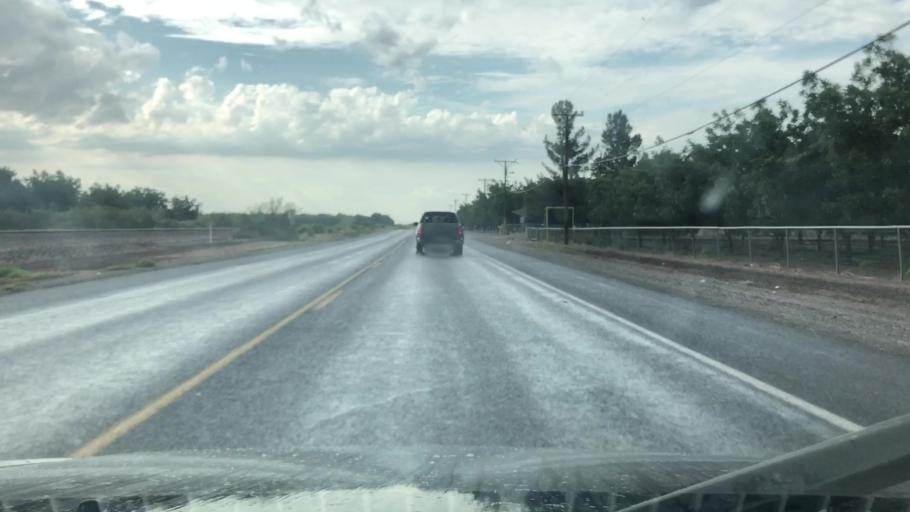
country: US
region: New Mexico
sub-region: Dona Ana County
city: Mesquite
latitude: 32.1935
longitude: -106.7148
